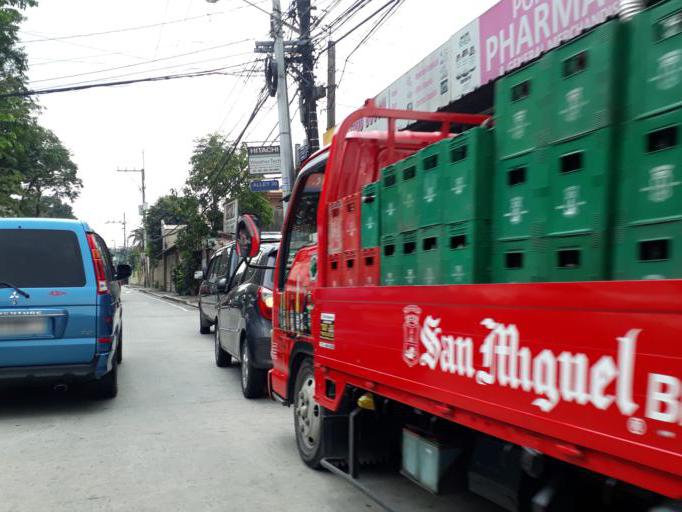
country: PH
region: Calabarzon
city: Bagong Pagasa
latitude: 14.6601
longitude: 121.0414
